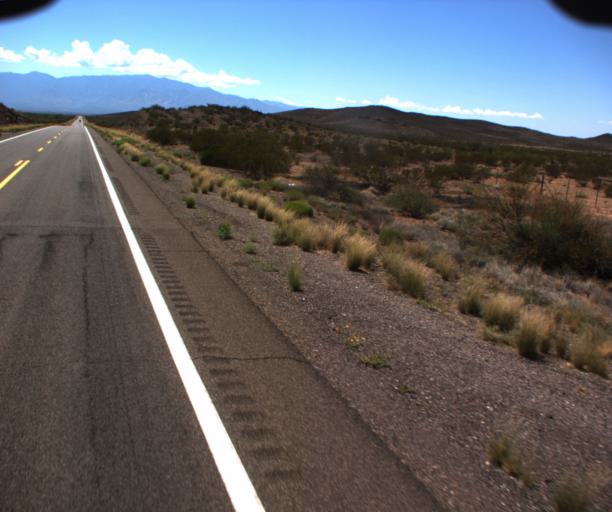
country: US
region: Arizona
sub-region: Graham County
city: Safford
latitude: 32.8100
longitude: -109.5037
